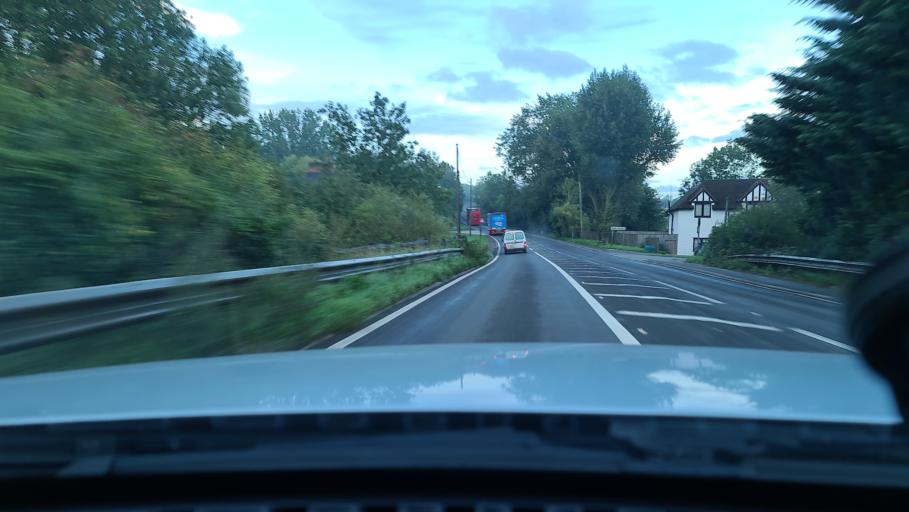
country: GB
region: England
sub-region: Warwickshire
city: Long Itchington
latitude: 52.2744
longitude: -1.3900
